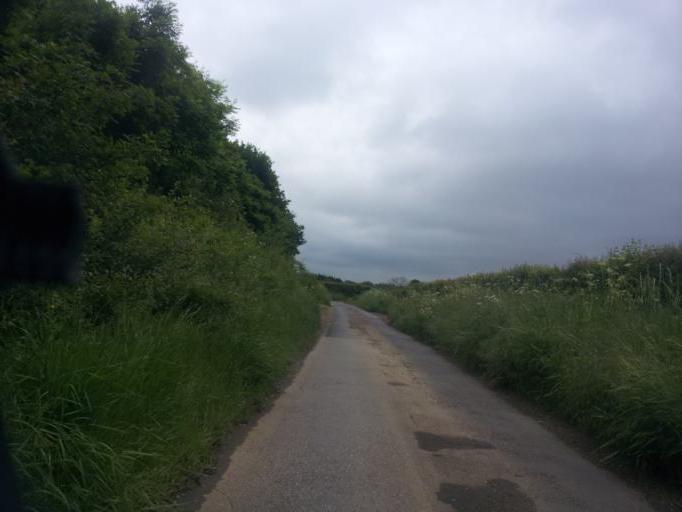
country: GB
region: England
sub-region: Kent
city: Yalding
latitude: 51.2144
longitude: 0.4297
